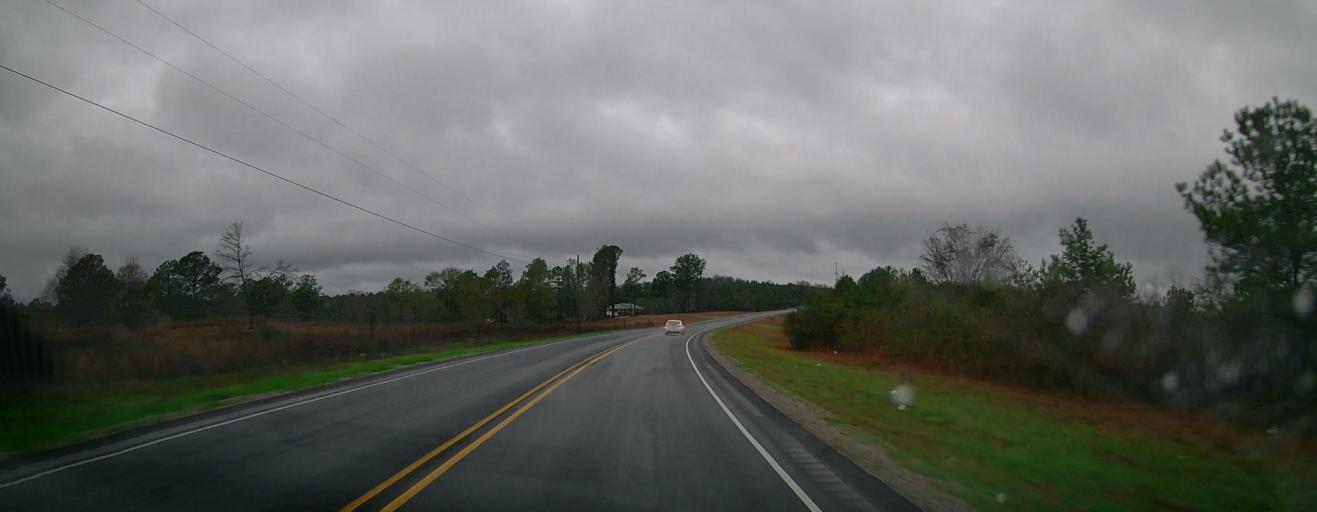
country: US
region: Alabama
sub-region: Chilton County
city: Clanton
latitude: 32.6311
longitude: -86.7453
